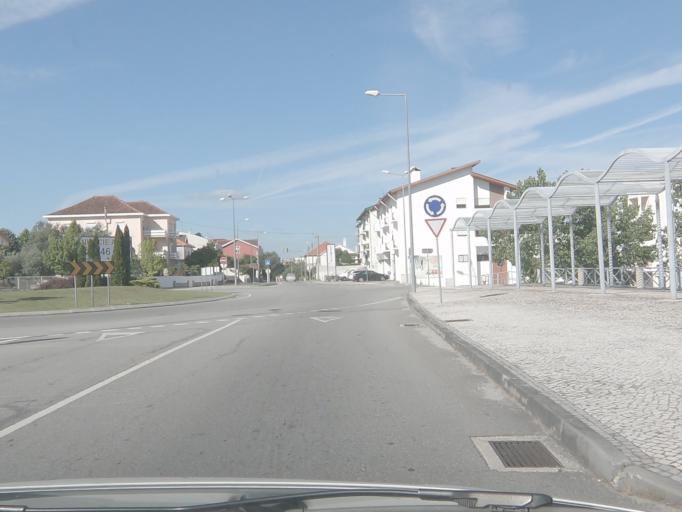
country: PT
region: Viseu
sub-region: Viseu
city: Viseu
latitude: 40.6386
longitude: -7.9279
